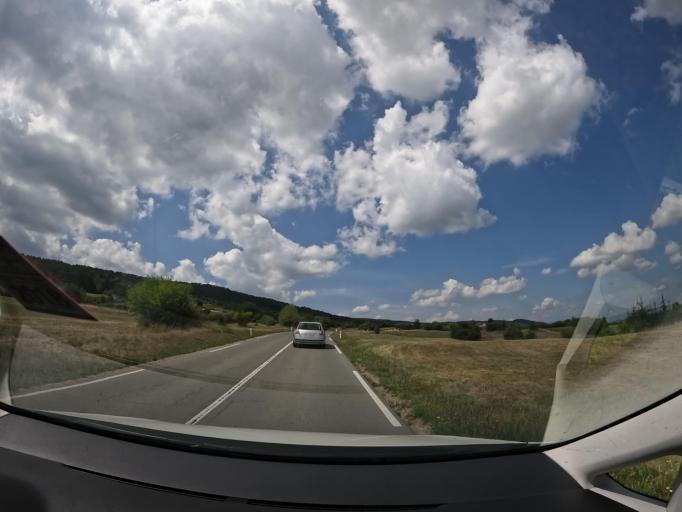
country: SI
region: Pivka
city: Pivka
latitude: 45.6273
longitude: 14.2344
